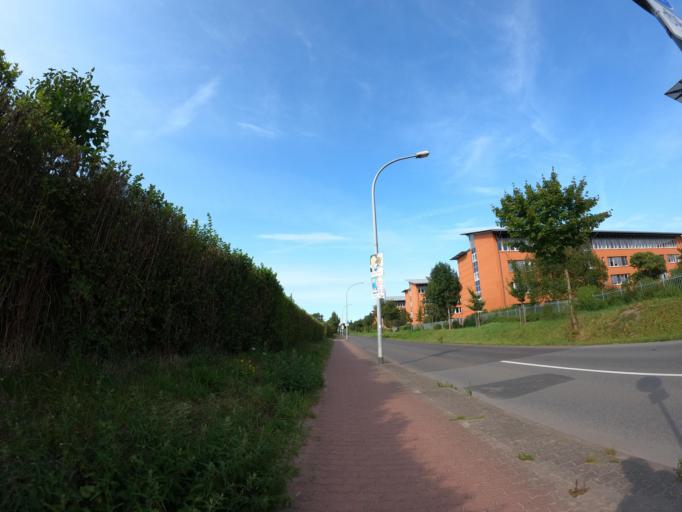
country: DE
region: Mecklenburg-Vorpommern
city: Kramerhof
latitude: 54.3375
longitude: 13.0654
